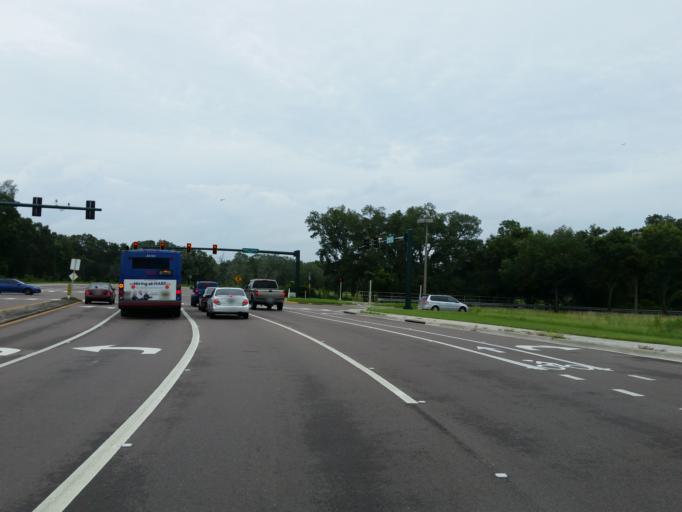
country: US
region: Florida
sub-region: Hillsborough County
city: Brandon
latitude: 27.9294
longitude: -82.3215
